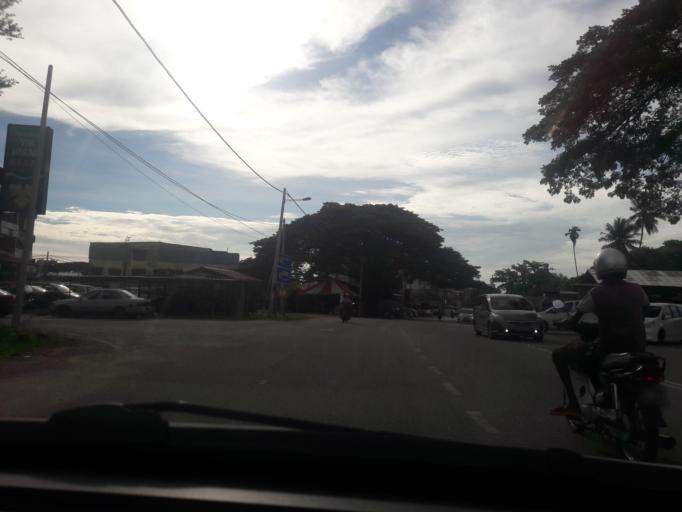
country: MY
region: Kedah
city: Sungai Petani
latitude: 5.6357
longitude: 100.4986
